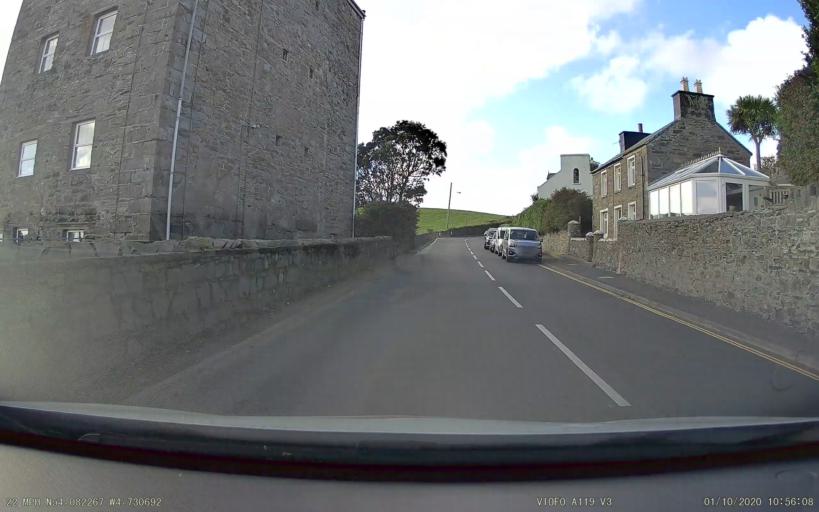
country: IM
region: Port Erin
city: Port Erin
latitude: 54.0825
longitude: -4.7309
